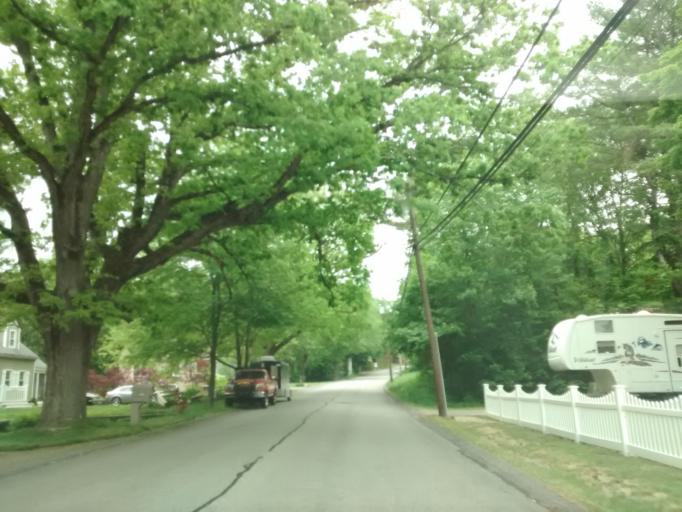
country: US
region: Rhode Island
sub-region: Providence County
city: Harrisville
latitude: 41.9622
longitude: -71.6668
